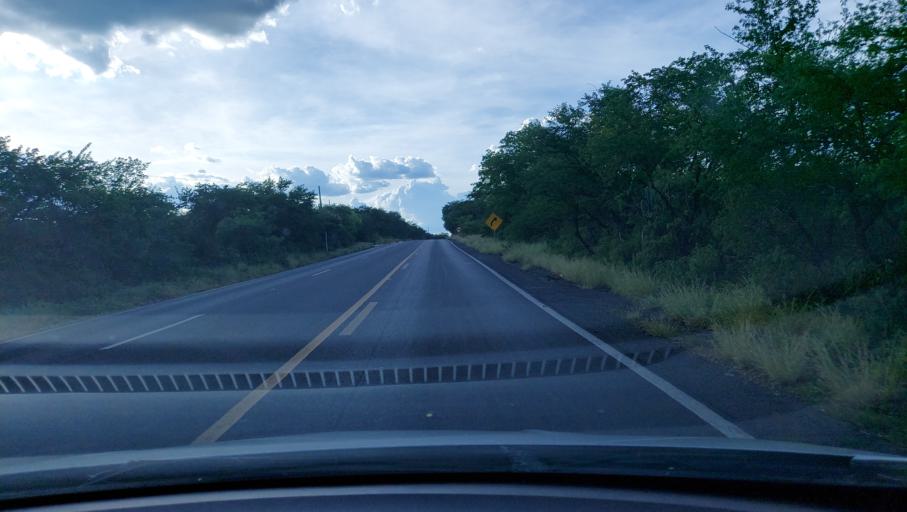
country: BR
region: Bahia
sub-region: Oliveira Dos Brejinhos
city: Beira Rio
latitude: -12.4011
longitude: -42.3927
